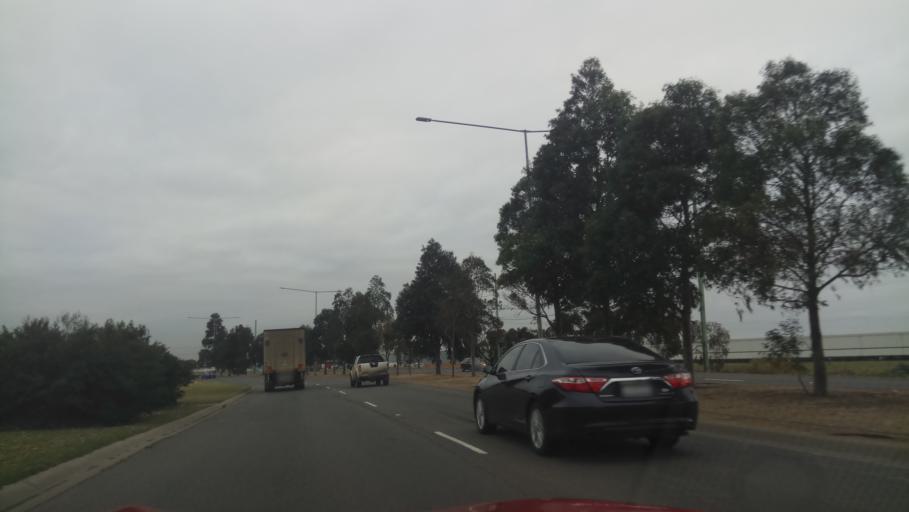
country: AU
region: Victoria
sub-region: Hobsons Bay
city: Altona
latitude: -37.8471
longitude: 144.8238
